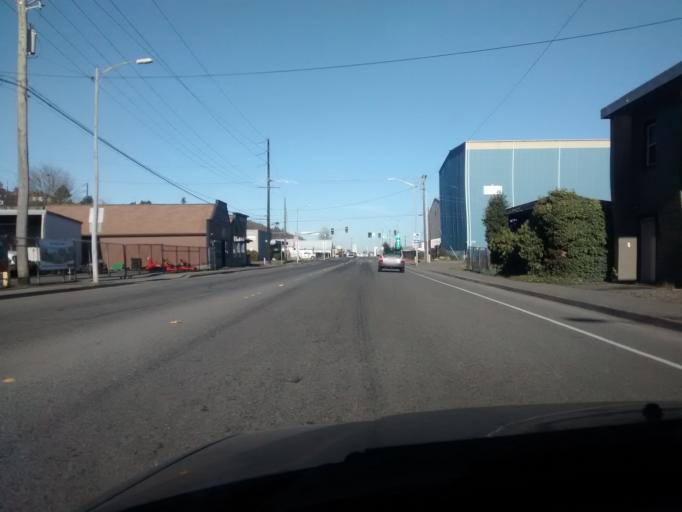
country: US
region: Washington
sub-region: Clallam County
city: Port Angeles
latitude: 48.1217
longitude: -123.4432
